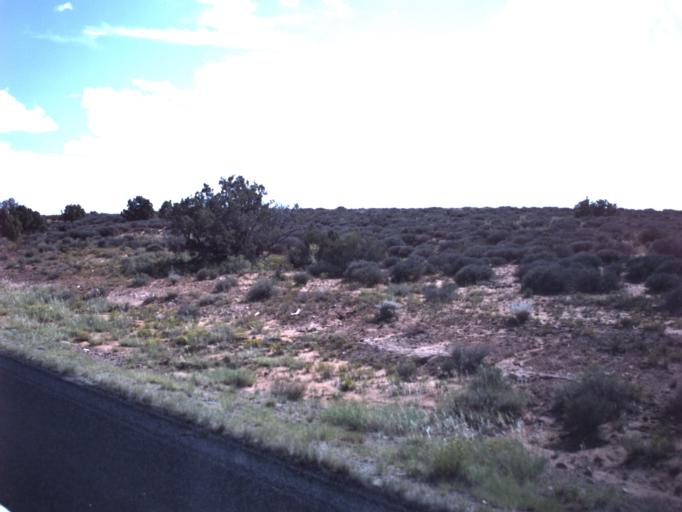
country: US
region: Utah
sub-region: Grand County
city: Moab
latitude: 38.5958
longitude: -109.8119
